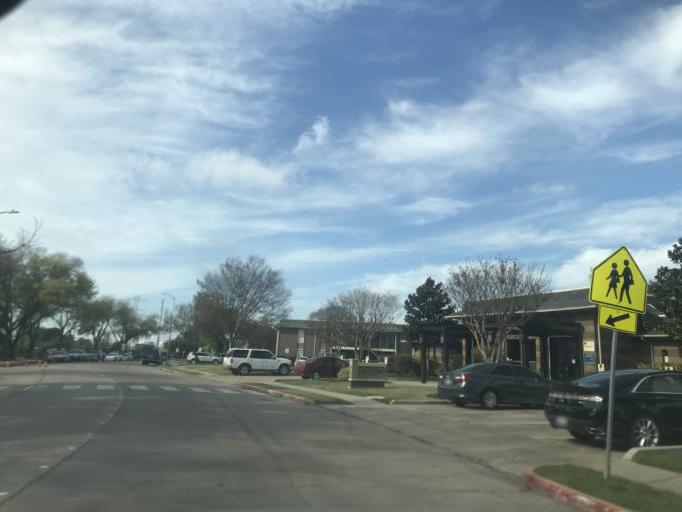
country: US
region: Texas
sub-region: Harris County
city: Bellaire
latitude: 29.7230
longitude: -95.4784
